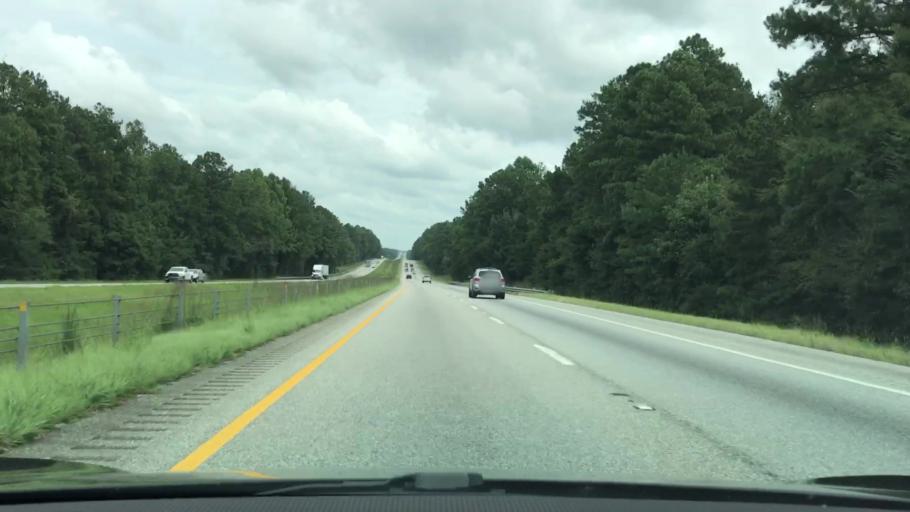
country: US
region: Alabama
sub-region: Chambers County
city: Huguley
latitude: 32.7790
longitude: -85.2507
